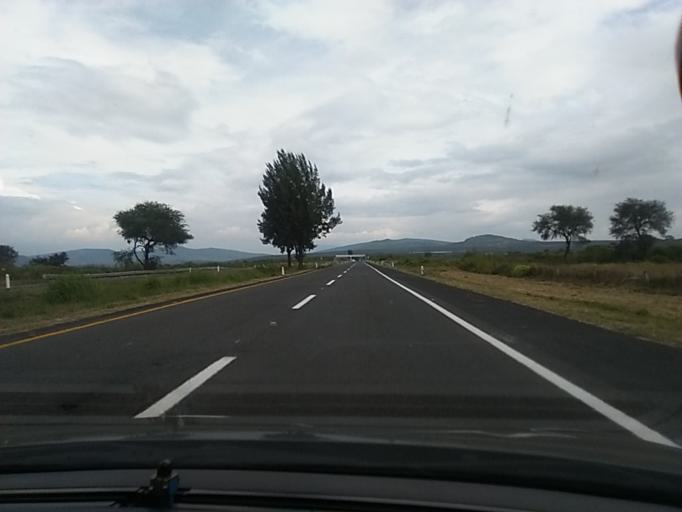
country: MX
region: Michoacan
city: Vistahermosa de Negrete
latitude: 20.2666
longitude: -102.4369
